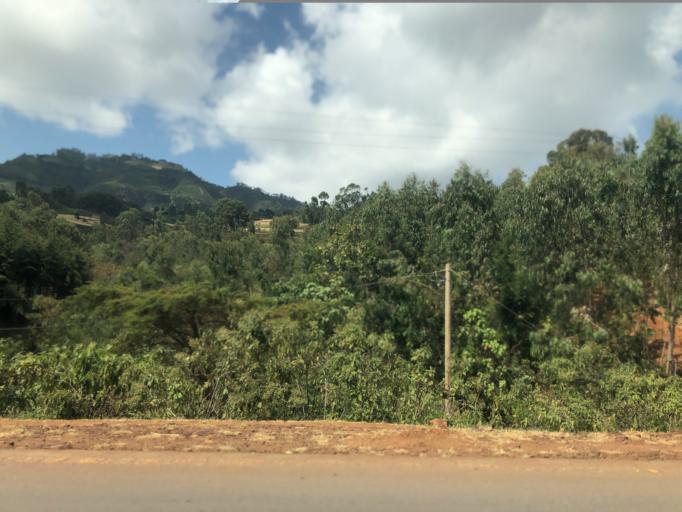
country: ET
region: Southern Nations, Nationalities, and People's Region
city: Boditi
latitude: 6.8935
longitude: 37.8066
